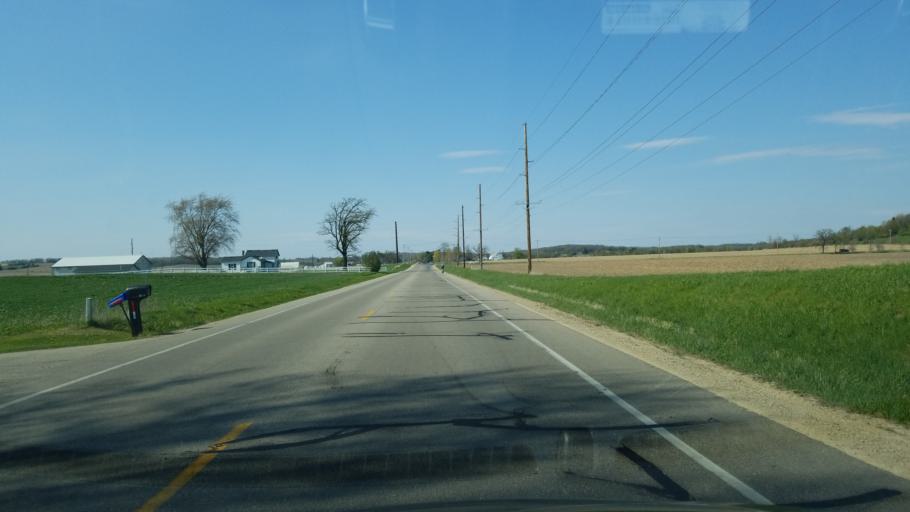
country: US
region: Wisconsin
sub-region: Dane County
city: Fitchburg
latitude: 42.9331
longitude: -89.4379
